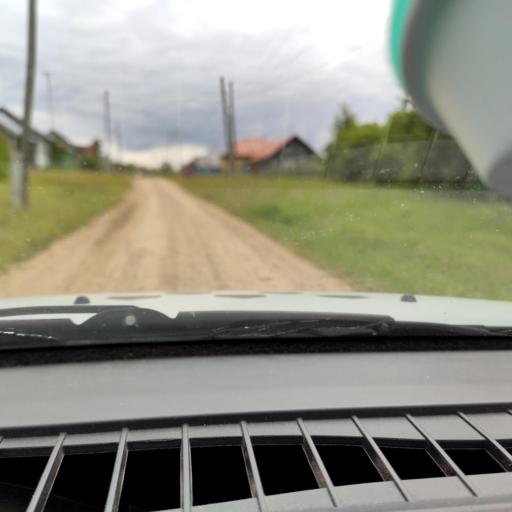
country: RU
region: Perm
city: Suksun
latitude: 57.2102
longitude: 57.7016
